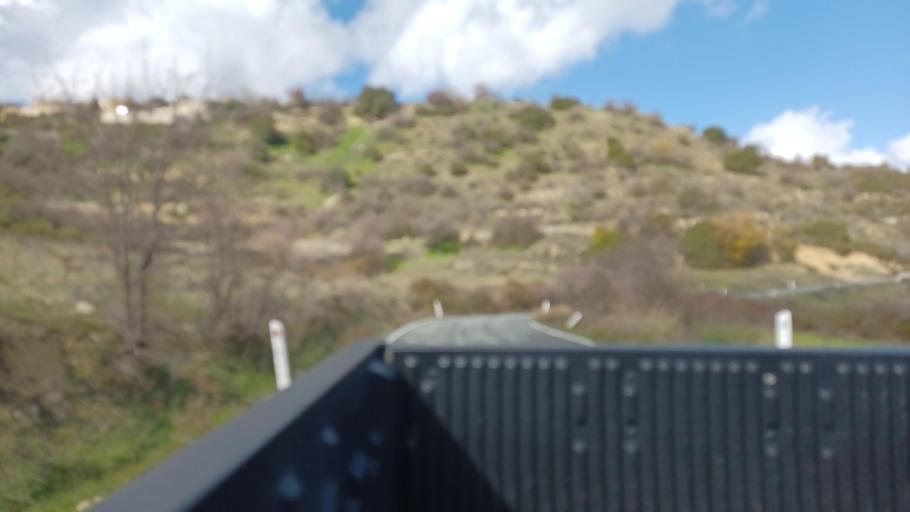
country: CY
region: Limassol
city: Pachna
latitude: 34.7797
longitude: 32.7421
